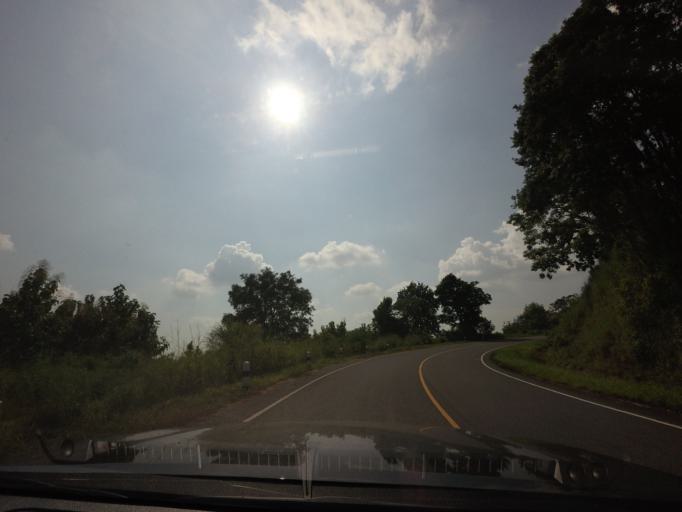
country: TH
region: Nan
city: Santi Suk
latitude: 18.9723
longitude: 100.9715
